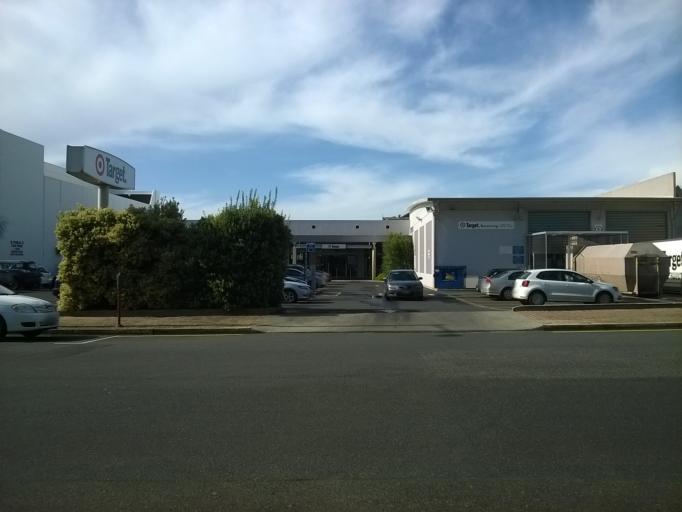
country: AU
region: Tasmania
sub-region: Burnie
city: Burnie
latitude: -41.0532
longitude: 145.9033
